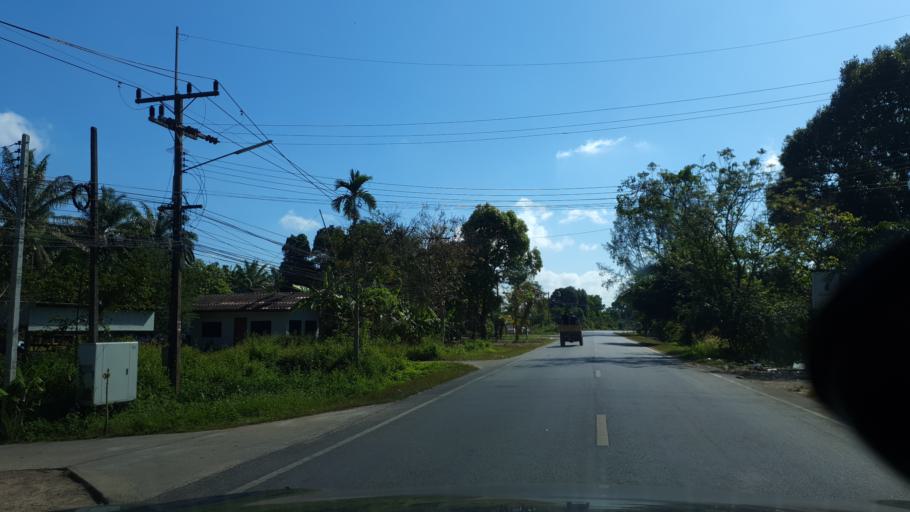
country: TH
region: Phangnga
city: Ban Ao Nang
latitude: 8.0301
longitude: 98.8651
